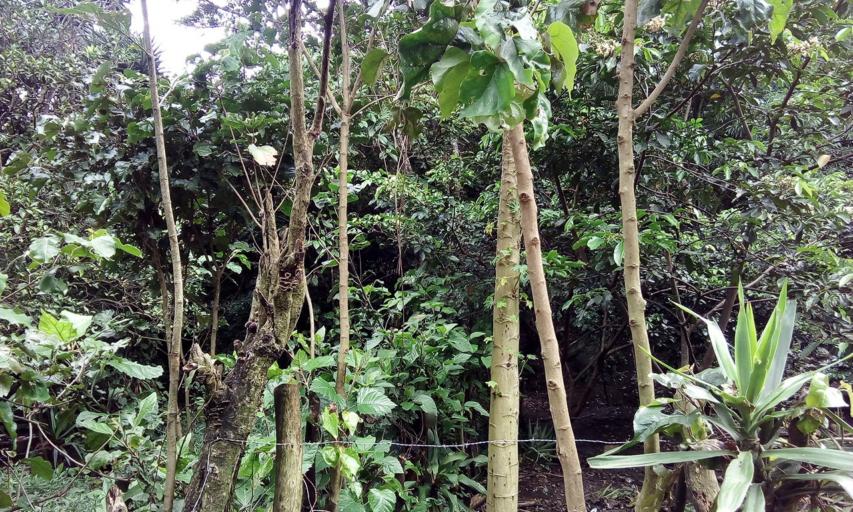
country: GT
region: Escuintla
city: San Vicente Pacaya
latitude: 14.3297
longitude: -90.6040
